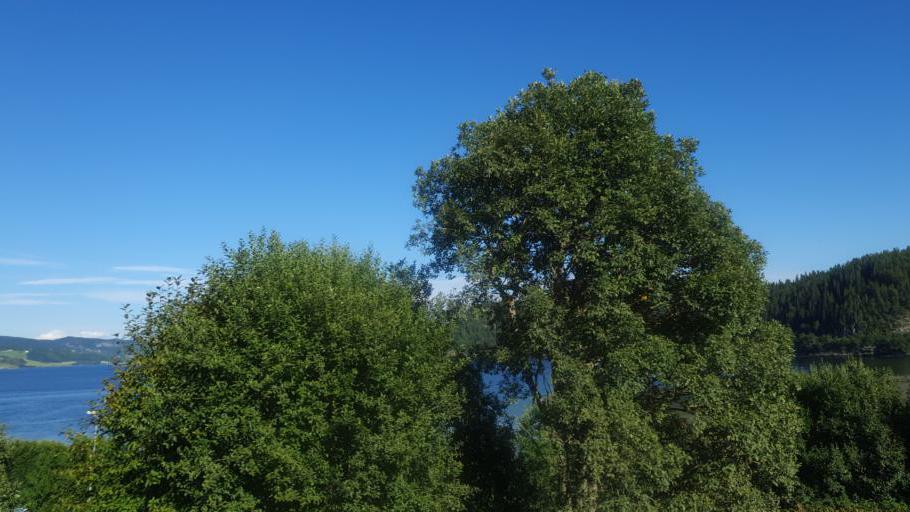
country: NO
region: Sor-Trondelag
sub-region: Skaun
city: Borsa
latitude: 63.3296
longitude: 10.0698
